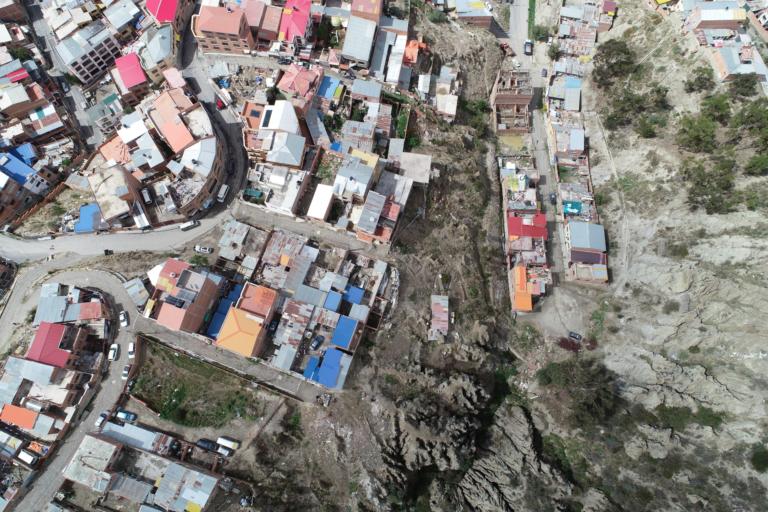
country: BO
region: La Paz
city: La Paz
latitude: -16.5169
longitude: -68.1081
